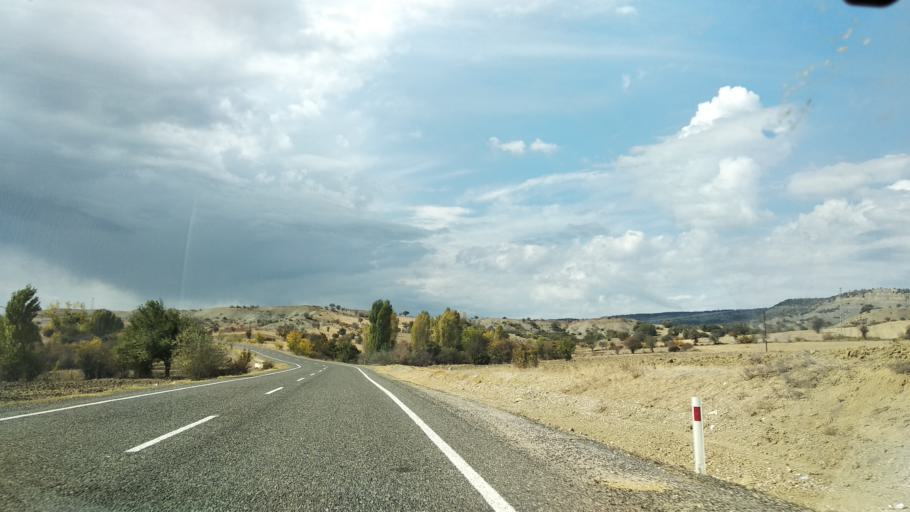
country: TR
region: Bolu
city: Seben
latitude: 40.3834
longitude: 31.5299
